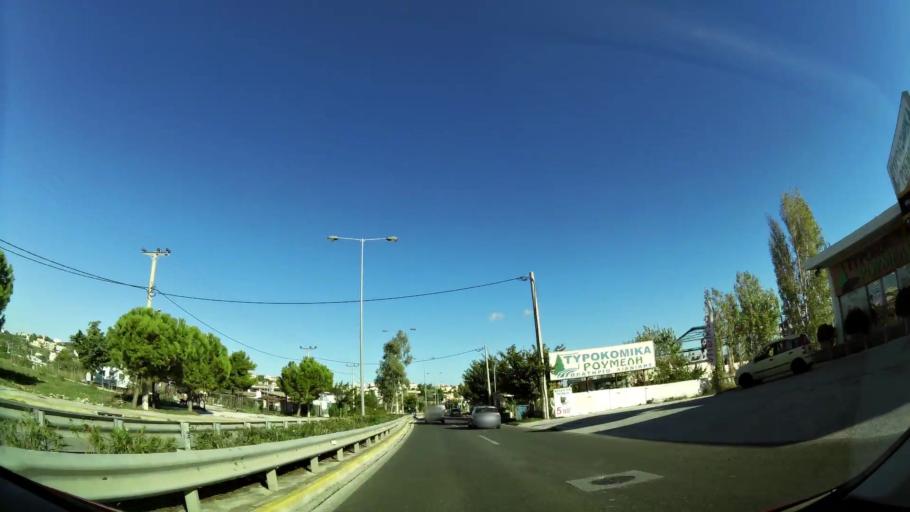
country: GR
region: Attica
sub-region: Nomarchia Anatolikis Attikis
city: Dhrafi
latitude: 38.0025
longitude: 23.9072
